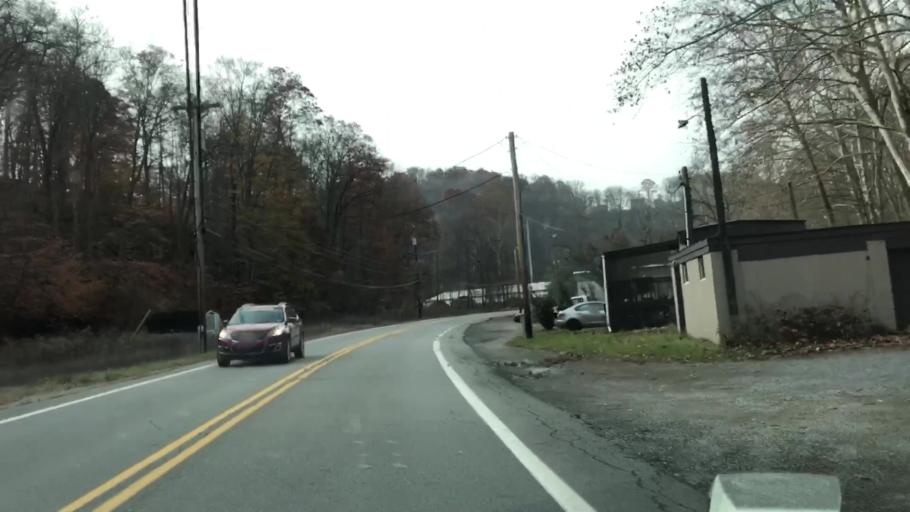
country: US
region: Pennsylvania
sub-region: Allegheny County
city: Carnot-Moon
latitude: 40.5319
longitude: -80.2303
